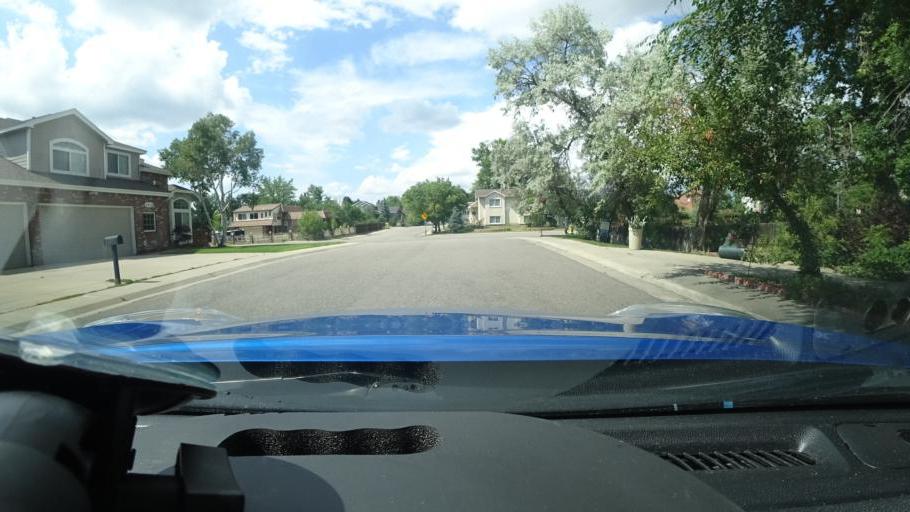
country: US
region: Colorado
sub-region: Adams County
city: Aurora
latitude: 39.6763
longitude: -104.8631
